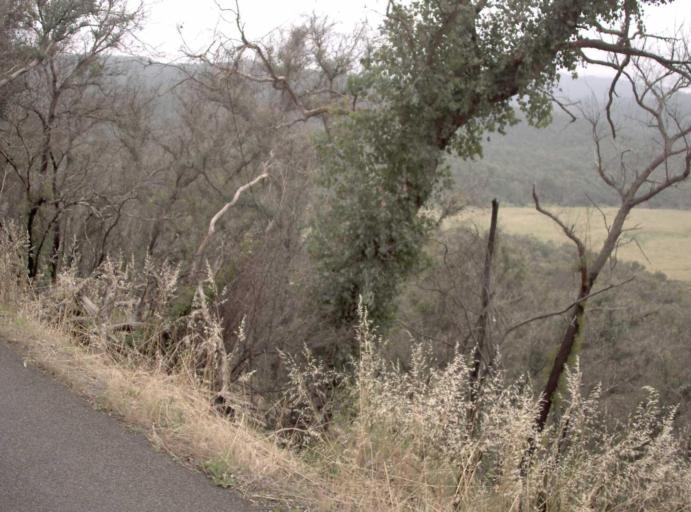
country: AU
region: Victoria
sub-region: Wellington
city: Heyfield
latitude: -37.8180
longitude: 146.6728
